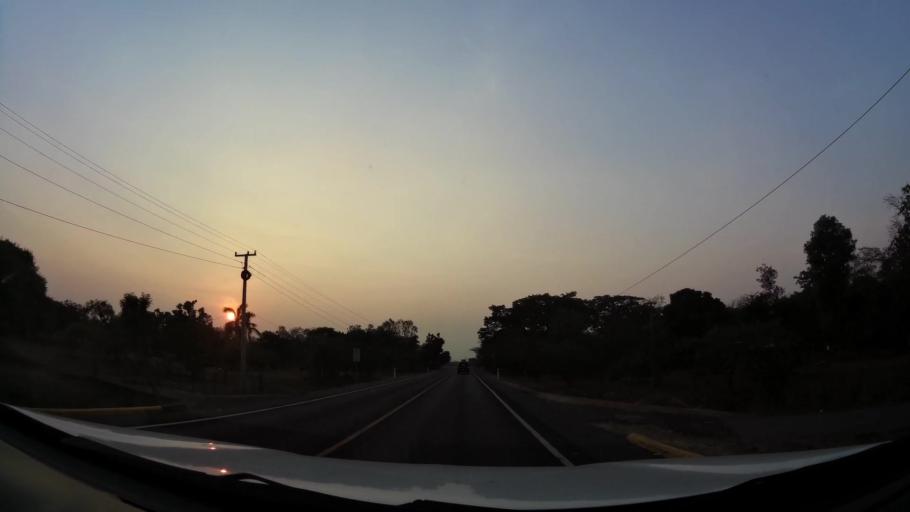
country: NI
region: Leon
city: Leon
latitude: 12.3492
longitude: -86.8262
